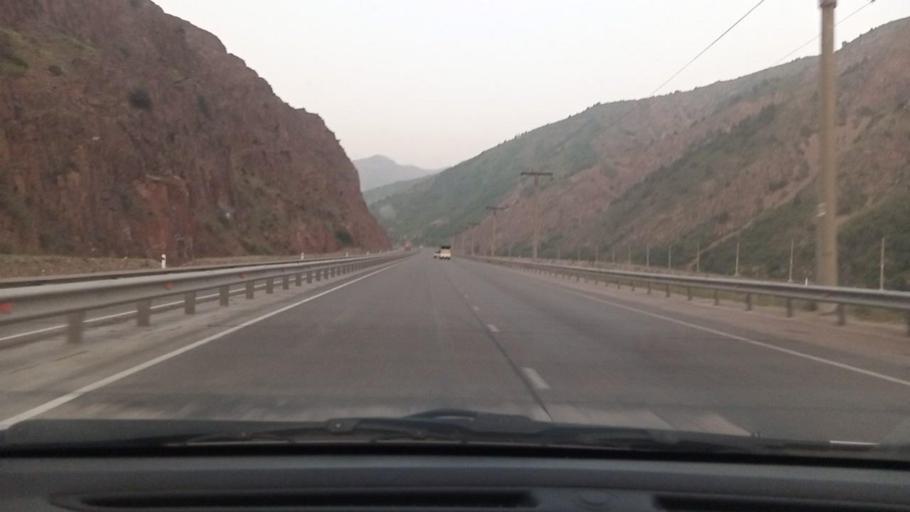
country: UZ
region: Toshkent
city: Angren
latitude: 41.1403
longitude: 70.3933
